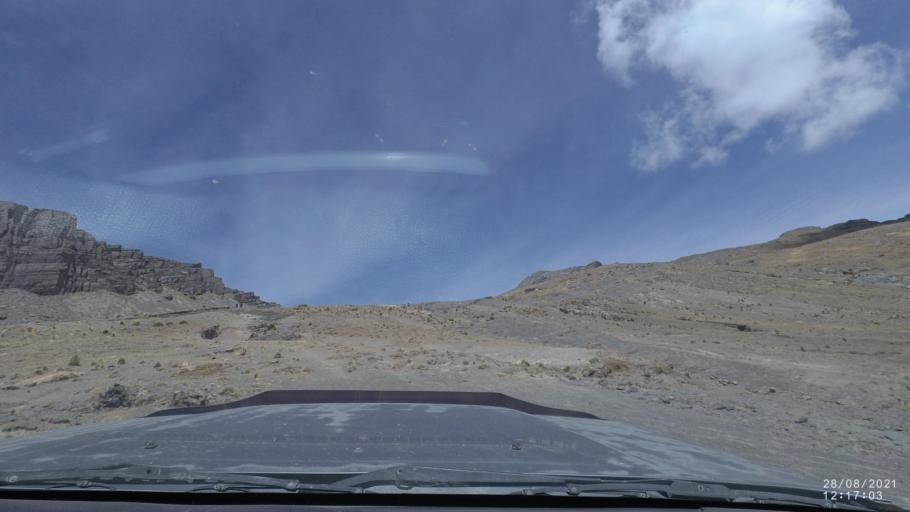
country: BO
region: Cochabamba
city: Sipe Sipe
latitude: -17.2773
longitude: -66.3811
